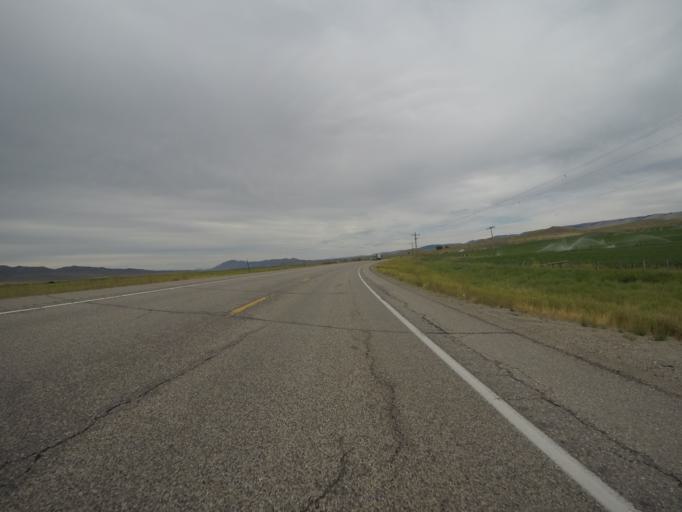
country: US
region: Utah
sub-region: Rich County
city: Randolph
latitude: 41.9901
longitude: -110.9419
